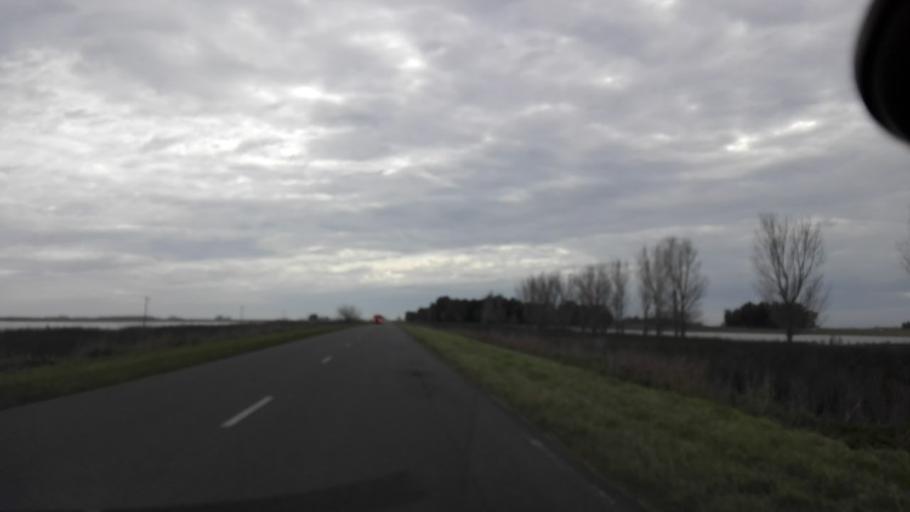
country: AR
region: Buenos Aires
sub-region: Partido de Las Flores
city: Las Flores
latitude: -36.3368
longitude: -59.0168
